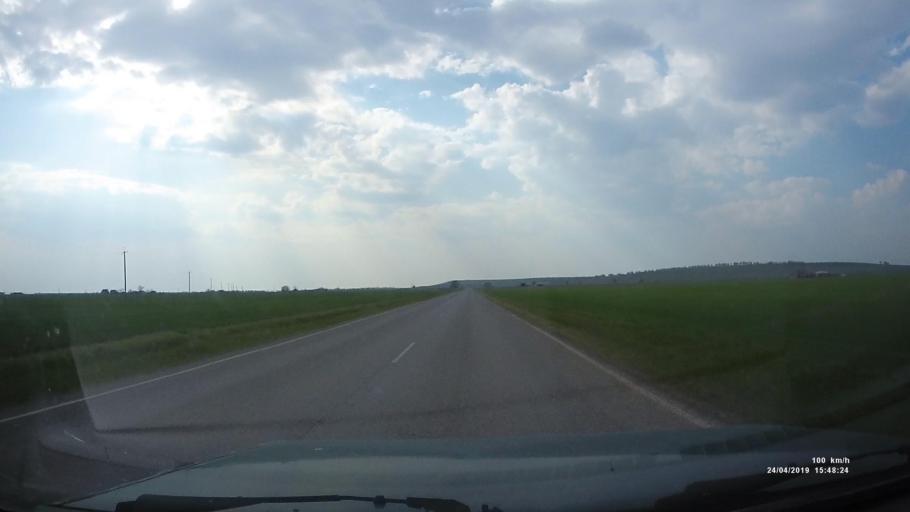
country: RU
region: Kalmykiya
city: Yashalta
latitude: 46.5984
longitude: 42.6768
